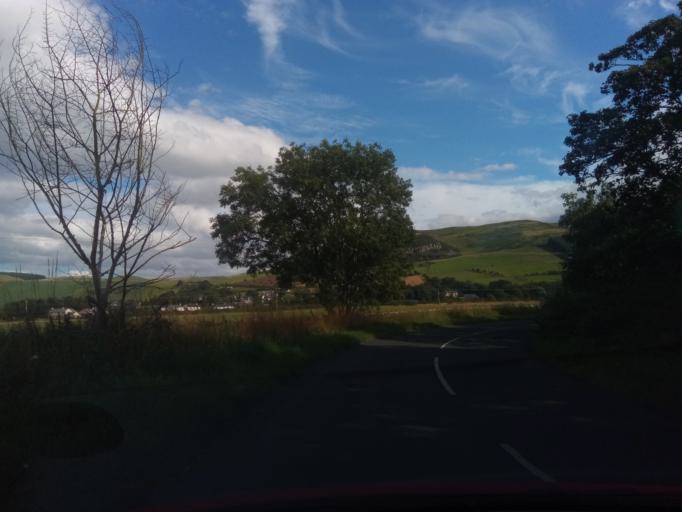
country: GB
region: Scotland
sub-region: The Scottish Borders
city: Coldstream
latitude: 55.5505
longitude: -2.2847
